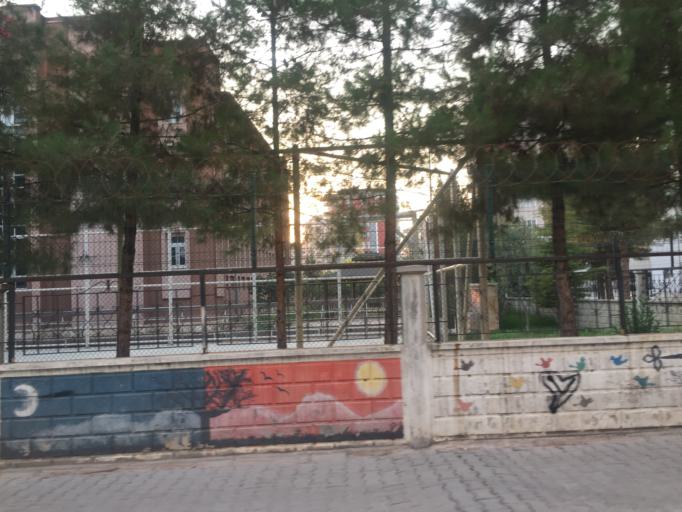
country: TR
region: Mardin
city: Midyat
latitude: 37.4311
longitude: 41.3392
